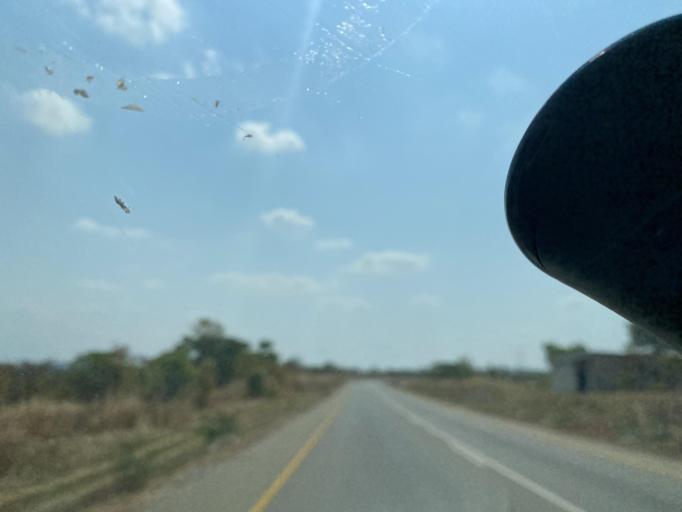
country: ZM
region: Lusaka
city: Chongwe
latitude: -15.5352
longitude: 28.6444
